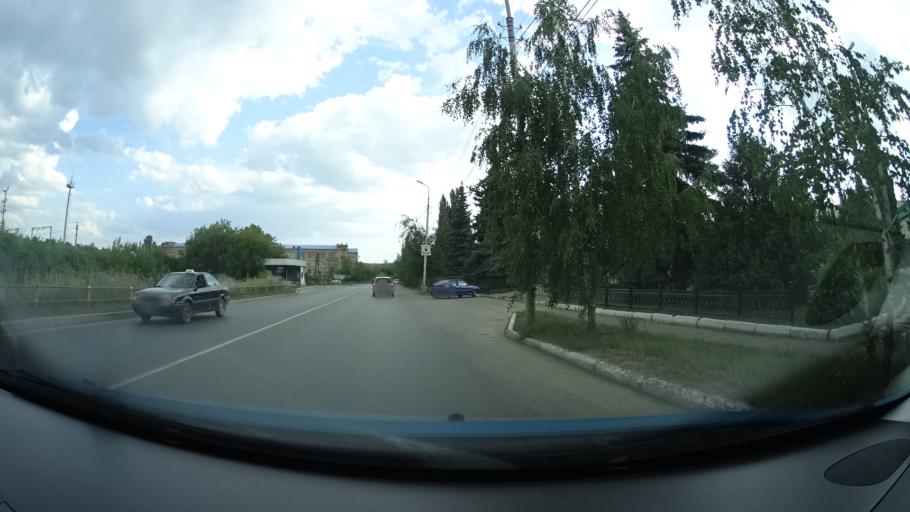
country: RU
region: Bashkortostan
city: Oktyabr'skiy
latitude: 54.4931
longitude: 53.4487
